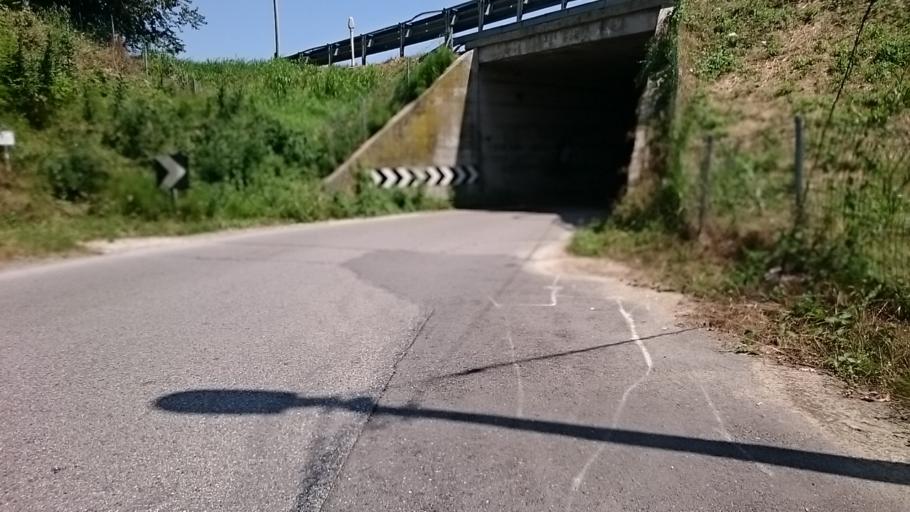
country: IT
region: Veneto
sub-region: Provincia di Padova
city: San Vito
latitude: 45.4230
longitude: 11.9600
